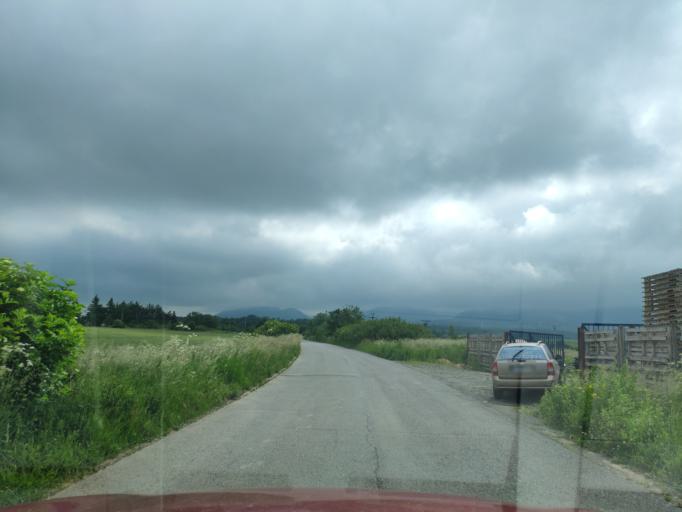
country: SK
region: Presovsky
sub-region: Okres Presov
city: Presov
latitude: 48.9969
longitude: 21.2972
